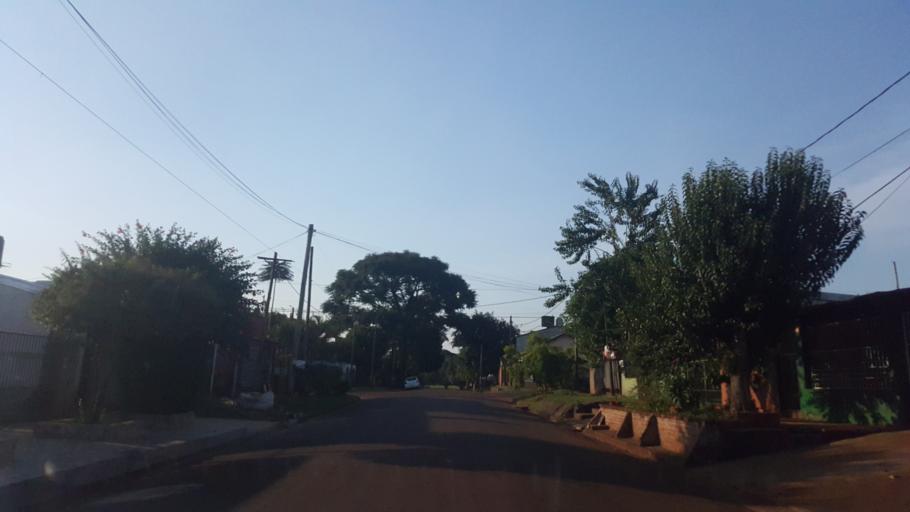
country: AR
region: Misiones
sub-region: Departamento de Capital
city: Posadas
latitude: -27.3912
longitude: -55.9180
